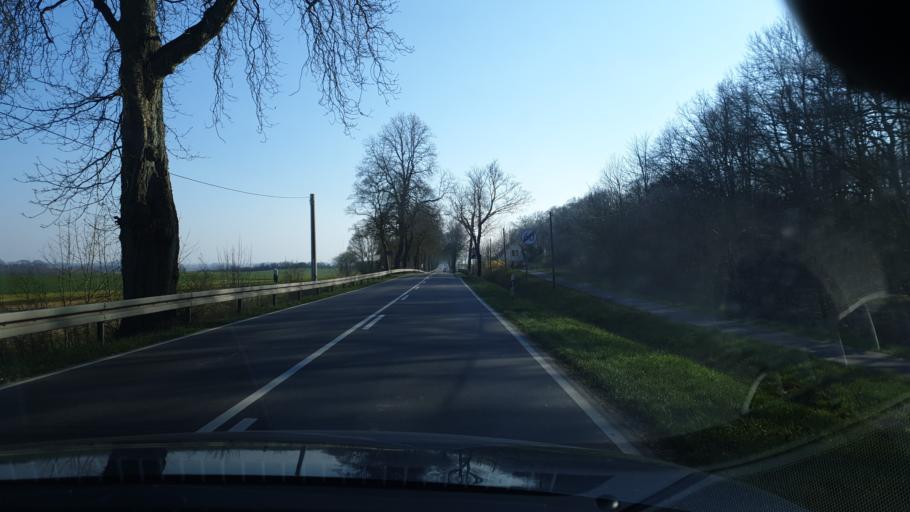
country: DE
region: Mecklenburg-Vorpommern
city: Lubstorf
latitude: 53.7172
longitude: 11.3993
